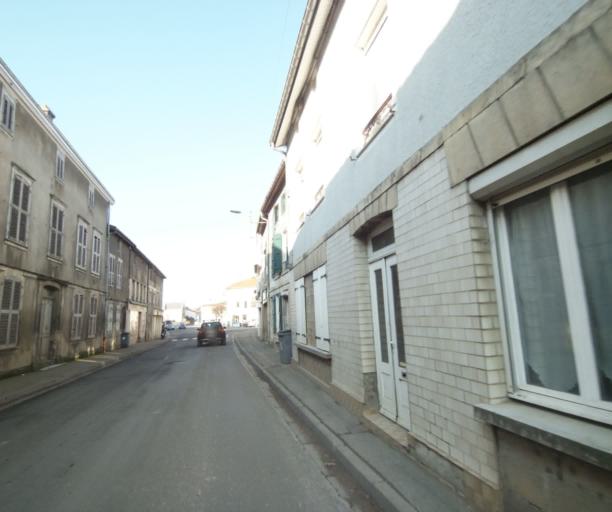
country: FR
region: Champagne-Ardenne
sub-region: Departement de la Haute-Marne
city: Wassy
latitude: 48.4971
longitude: 4.9497
